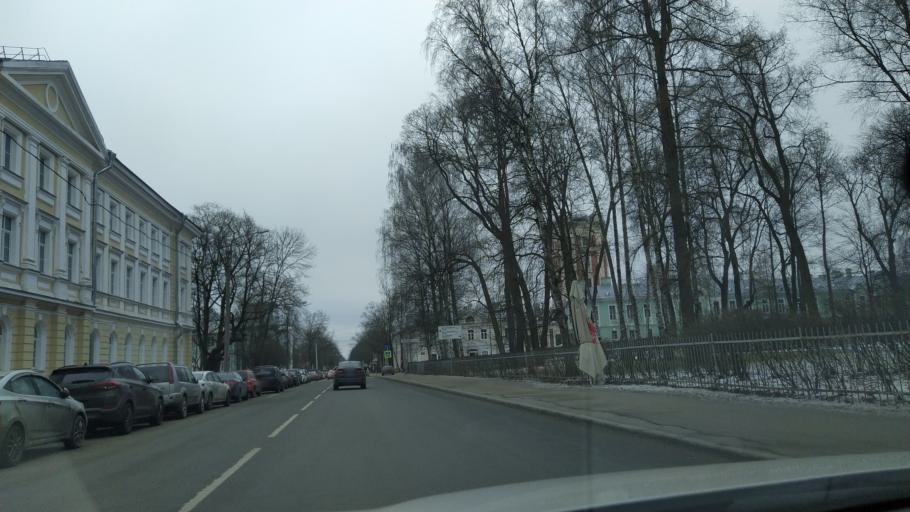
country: RU
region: St.-Petersburg
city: Pushkin
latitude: 59.7190
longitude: 30.3973
